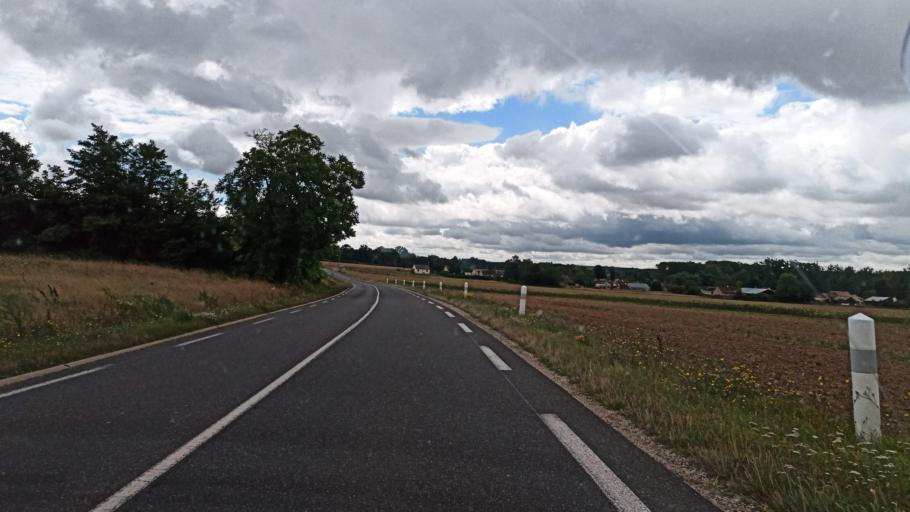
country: FR
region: Ile-de-France
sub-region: Departement de Seine-et-Marne
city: Voulx
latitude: 48.3123
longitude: 2.9476
